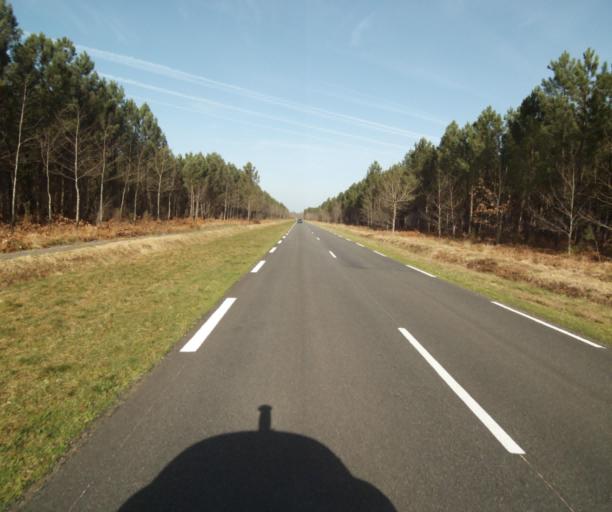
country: FR
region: Aquitaine
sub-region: Departement de la Gironde
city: Grignols
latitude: 44.1887
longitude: -0.1105
